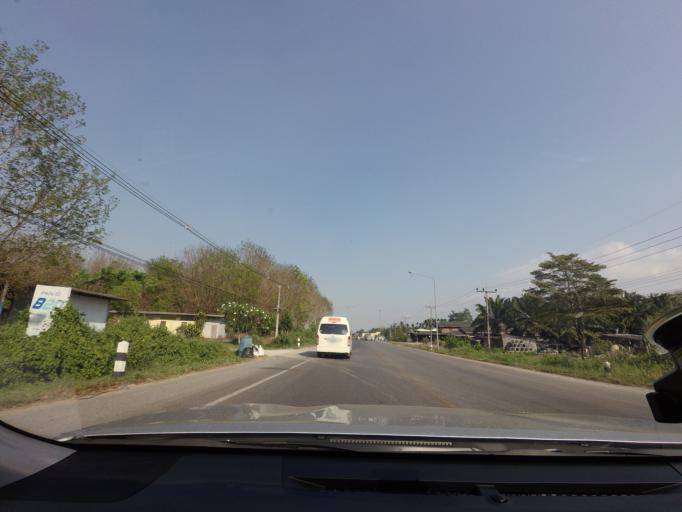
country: TH
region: Surat Thani
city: Phrasaeng
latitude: 8.5732
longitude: 99.2233
